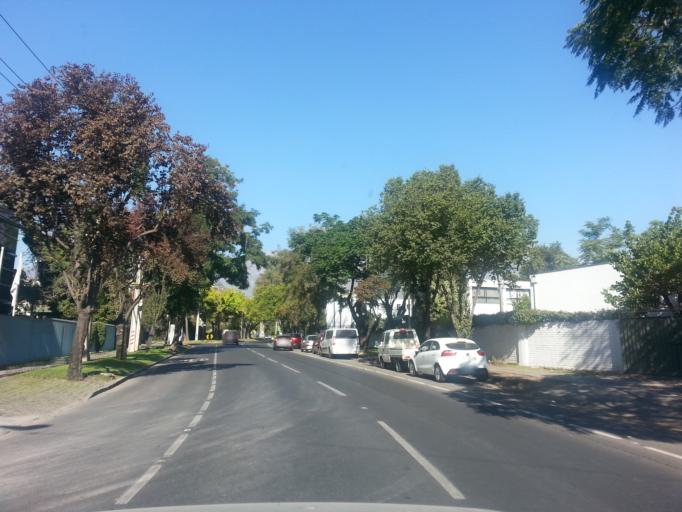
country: CL
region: Santiago Metropolitan
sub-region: Provincia de Santiago
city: Villa Presidente Frei, Nunoa, Santiago, Chile
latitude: -33.4259
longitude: -70.5760
